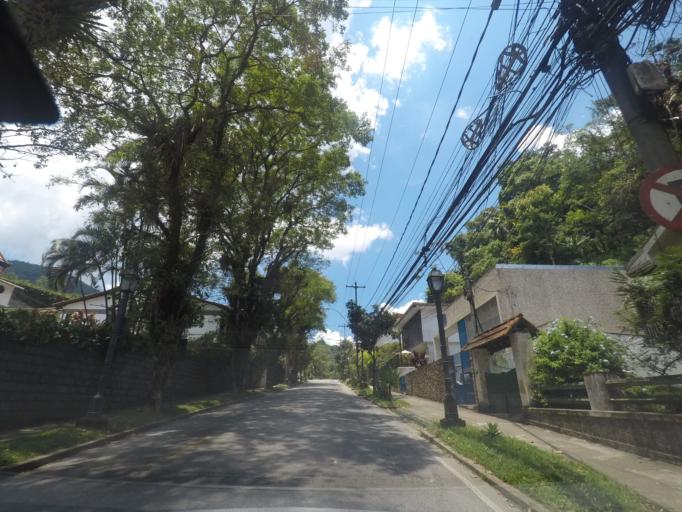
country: BR
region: Rio de Janeiro
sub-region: Petropolis
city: Petropolis
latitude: -22.5060
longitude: -43.1727
